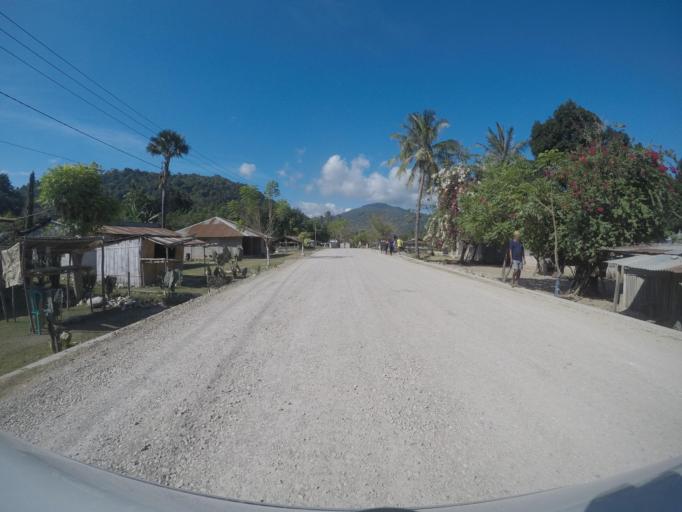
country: TL
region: Viqueque
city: Viqueque
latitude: -8.8051
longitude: 126.5457
